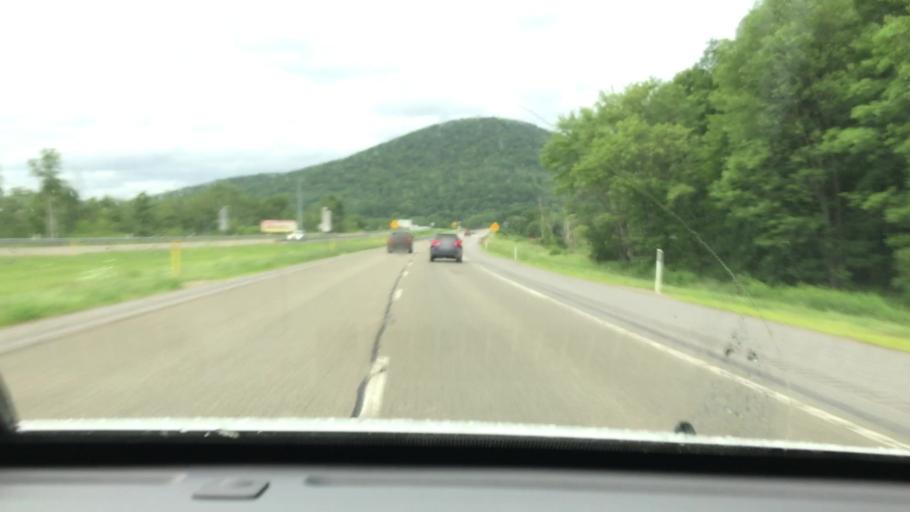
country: US
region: Pennsylvania
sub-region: McKean County
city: Foster Brook
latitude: 41.9941
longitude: -78.6208
